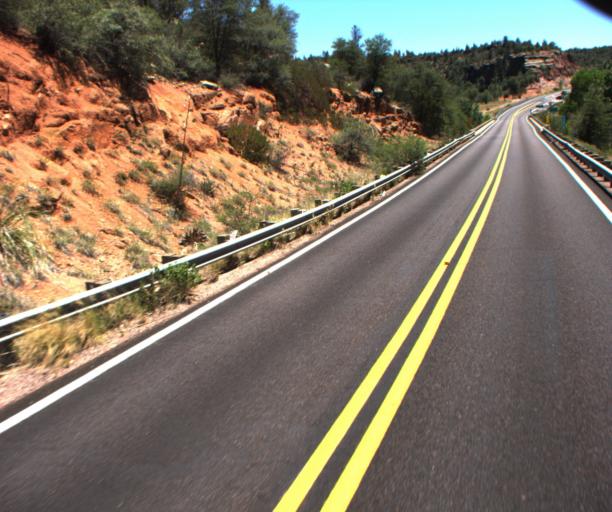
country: US
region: Arizona
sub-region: Gila County
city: Payson
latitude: 34.3023
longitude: -111.3585
